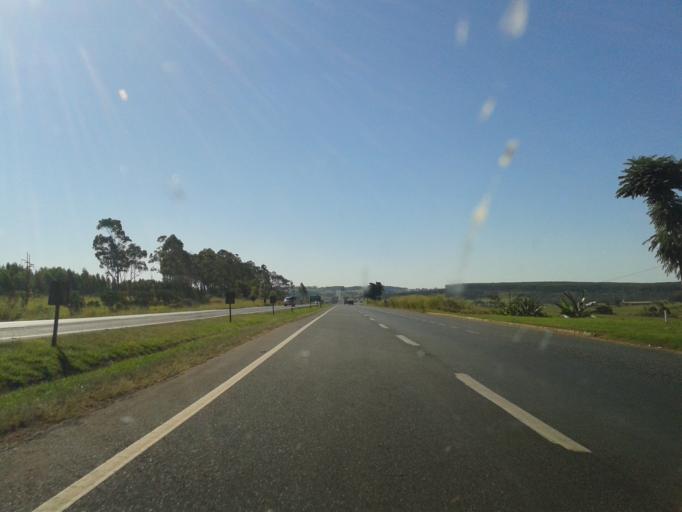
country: BR
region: Minas Gerais
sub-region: Uberaba
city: Uberaba
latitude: -19.5836
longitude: -48.0311
